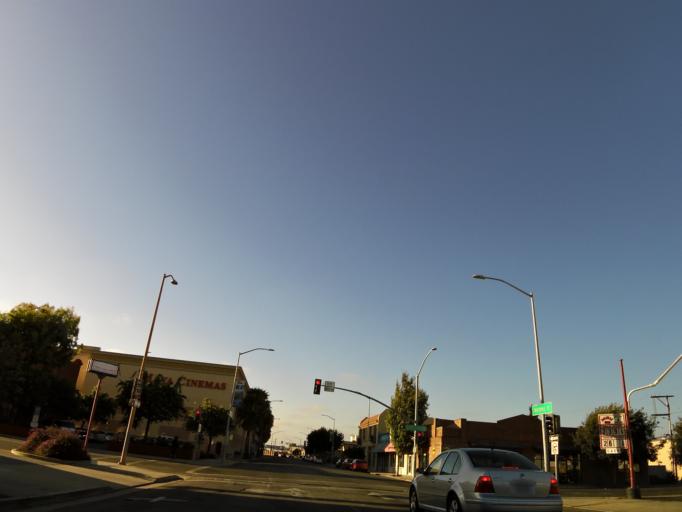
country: US
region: California
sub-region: Monterey County
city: Salinas
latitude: 36.6755
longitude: -121.6541
